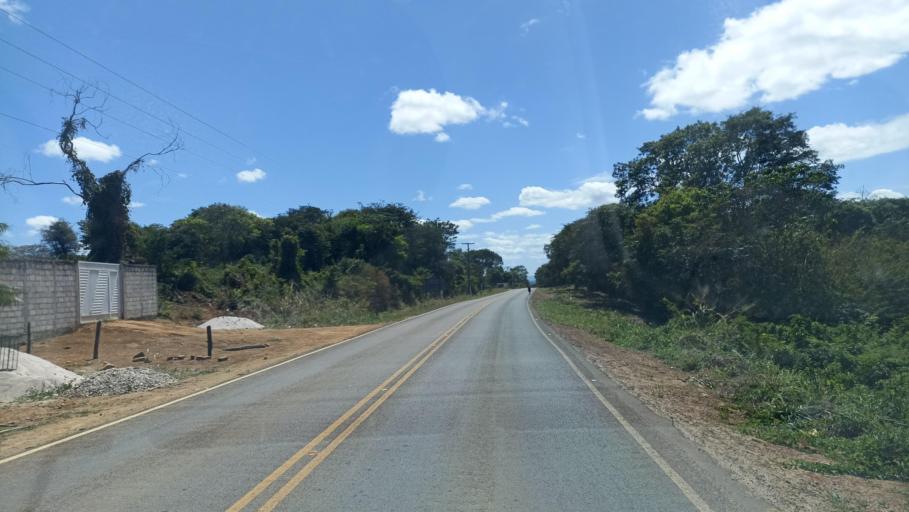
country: BR
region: Bahia
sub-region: Andarai
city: Vera Cruz
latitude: -12.7909
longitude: -41.3286
